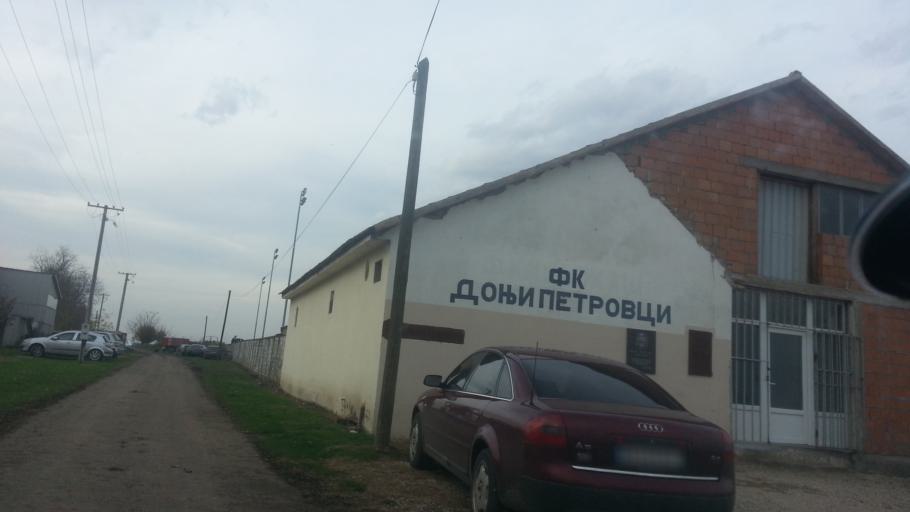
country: RS
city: Putinci
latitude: 44.9672
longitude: 19.9810
